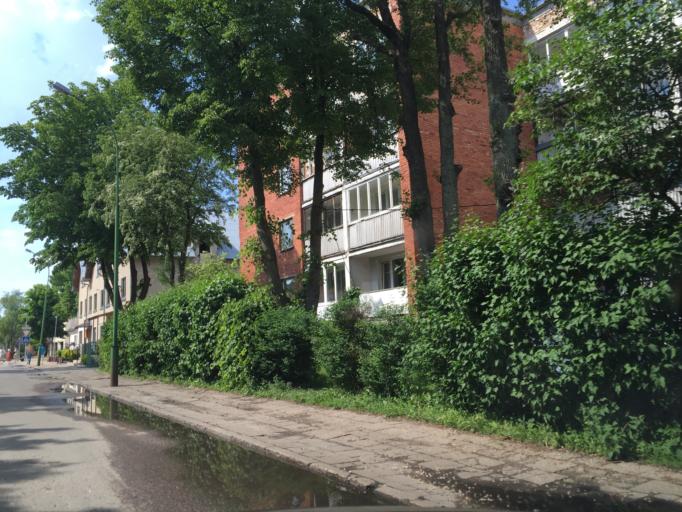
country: LT
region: Klaipedos apskritis
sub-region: Klaipeda
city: Palanga
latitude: 55.9230
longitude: 21.0711
